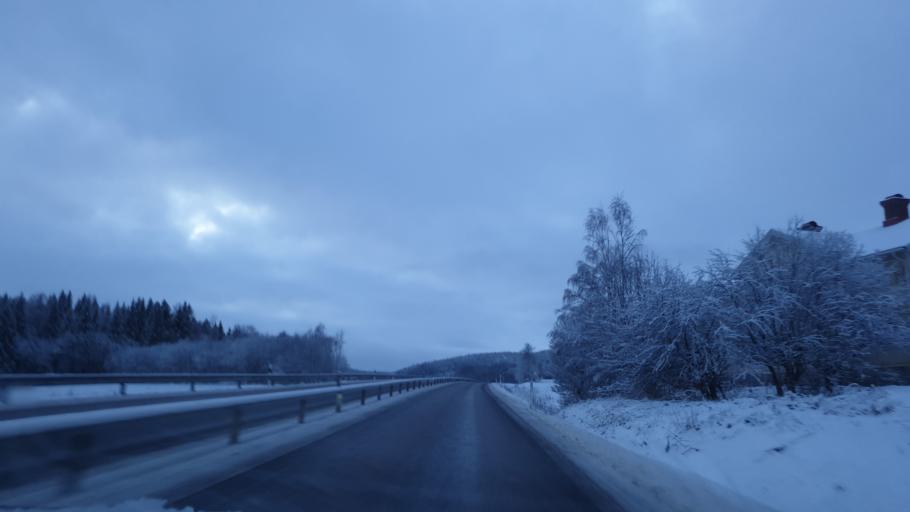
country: SE
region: Vaesternorrland
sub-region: Kramfors Kommun
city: Nordingra
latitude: 63.0305
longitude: 18.3116
